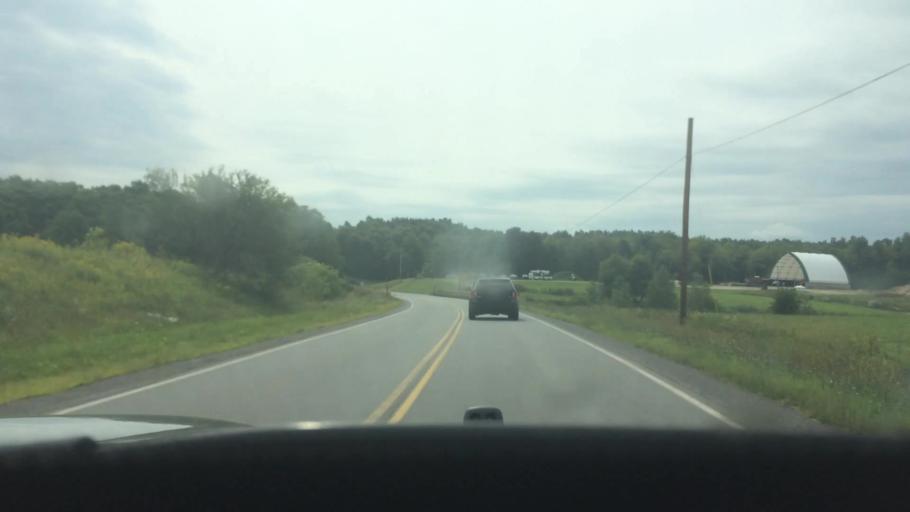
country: US
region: New York
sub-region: St. Lawrence County
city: Canton
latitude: 44.4730
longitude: -75.2388
